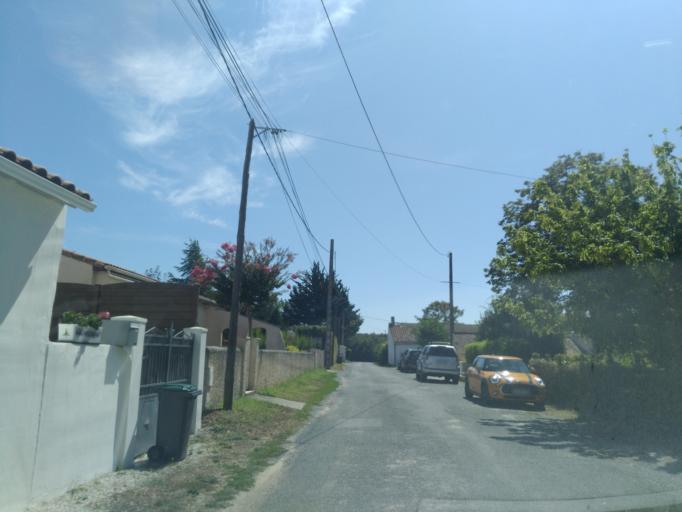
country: FR
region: Poitou-Charentes
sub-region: Departement de la Charente-Maritime
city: Breuillet
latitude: 45.6923
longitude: -1.0750
